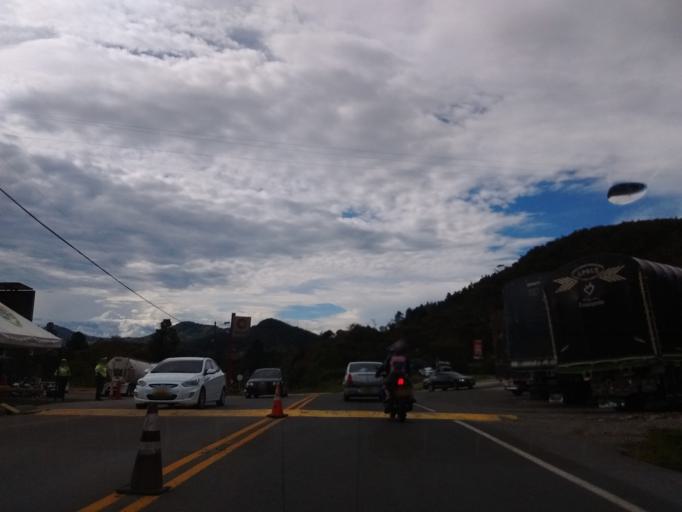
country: CO
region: Antioquia
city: Santuario
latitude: 6.1133
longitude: -75.2308
